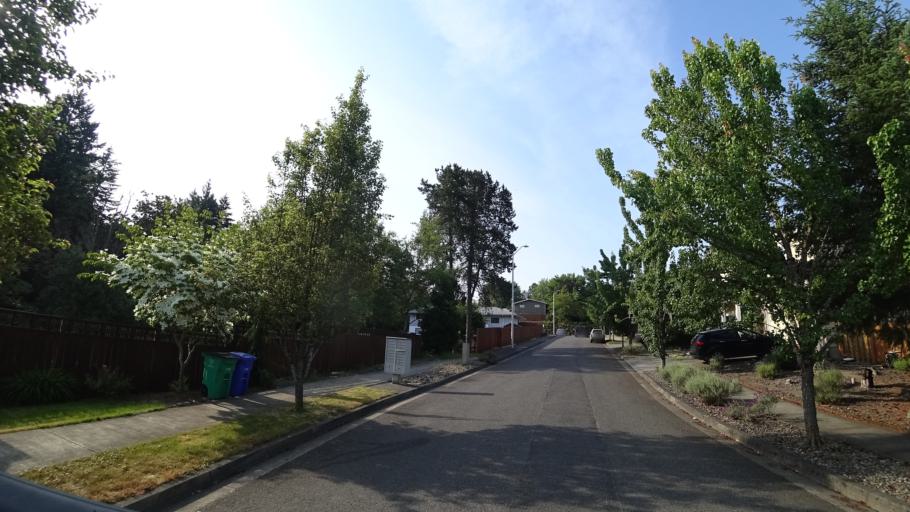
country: US
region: Oregon
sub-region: Clackamas County
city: Happy Valley
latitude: 45.4621
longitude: -122.5258
